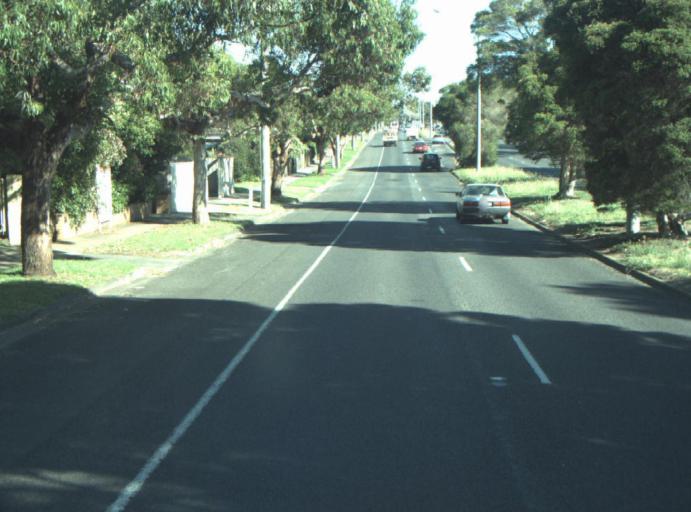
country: AU
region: Victoria
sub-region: Greater Geelong
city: Hamlyn Heights
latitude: -38.1218
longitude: 144.3350
